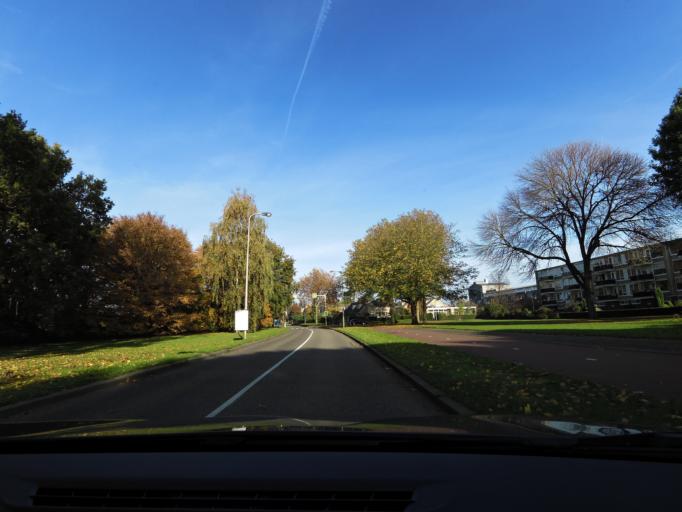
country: NL
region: South Holland
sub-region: Gemeente Ridderkerk
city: Ridderkerk
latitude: 51.8825
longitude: 4.5964
